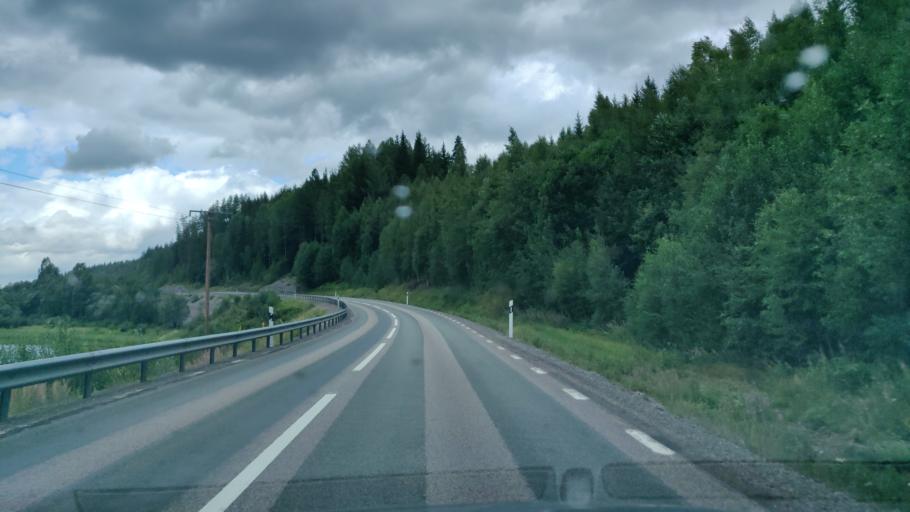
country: SE
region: Vaermland
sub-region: Torsby Kommun
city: Torsby
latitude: 60.5453
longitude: 13.1175
